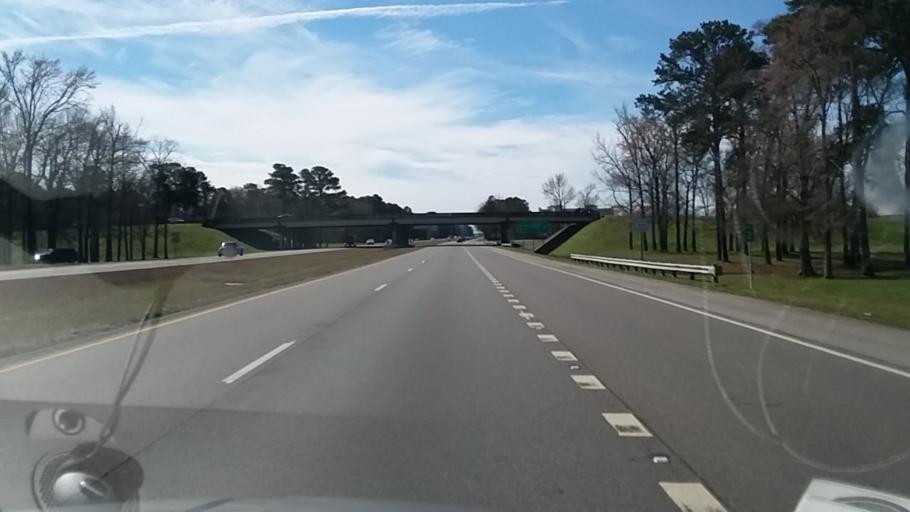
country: US
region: Alabama
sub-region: Madison County
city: Redstone Arsenal
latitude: 34.7298
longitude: -86.6703
